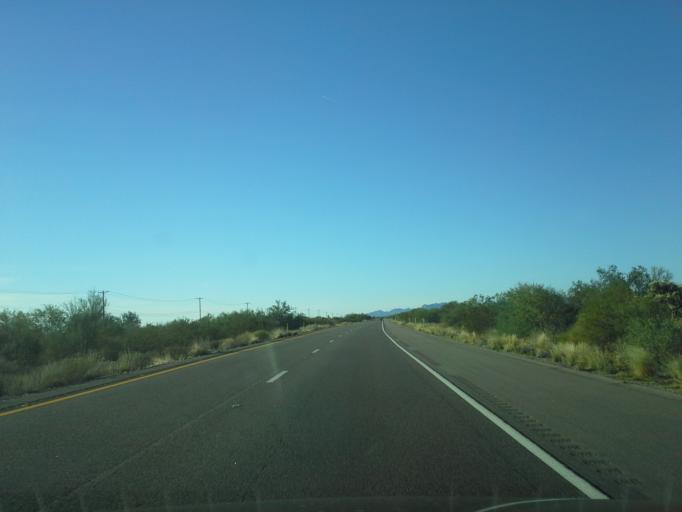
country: US
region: Arizona
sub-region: Pinal County
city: Gold Camp
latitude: 33.3101
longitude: -111.4098
